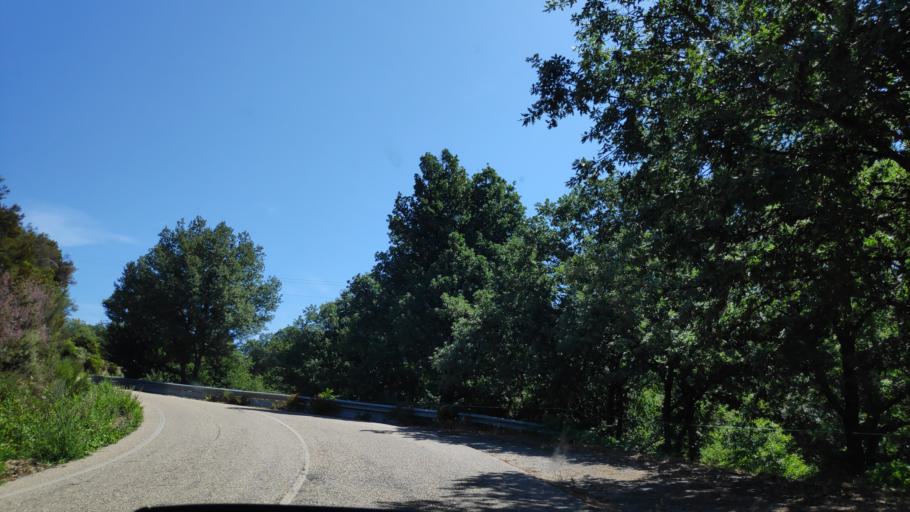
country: ES
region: Castille and Leon
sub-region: Provincia de Zamora
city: Cobreros
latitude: 42.0249
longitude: -6.6855
